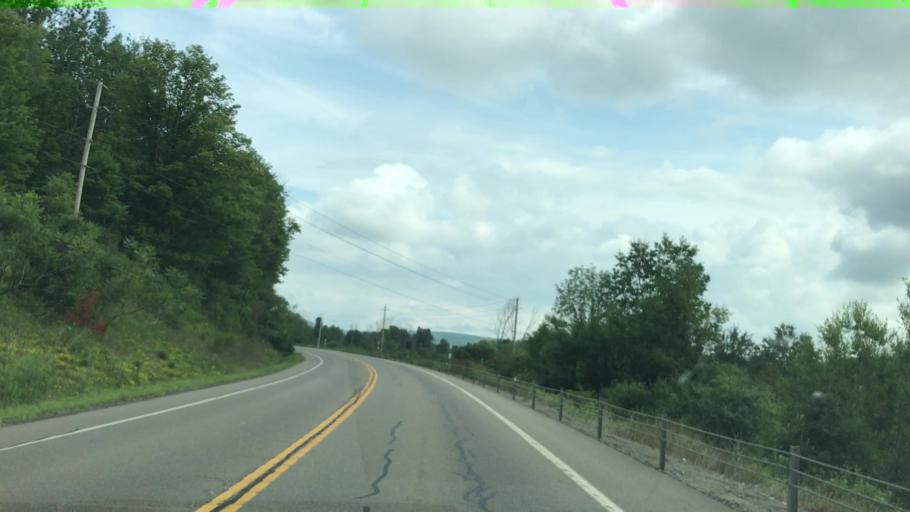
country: US
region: New York
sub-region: Steuben County
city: Bath
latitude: 42.4635
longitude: -77.3027
